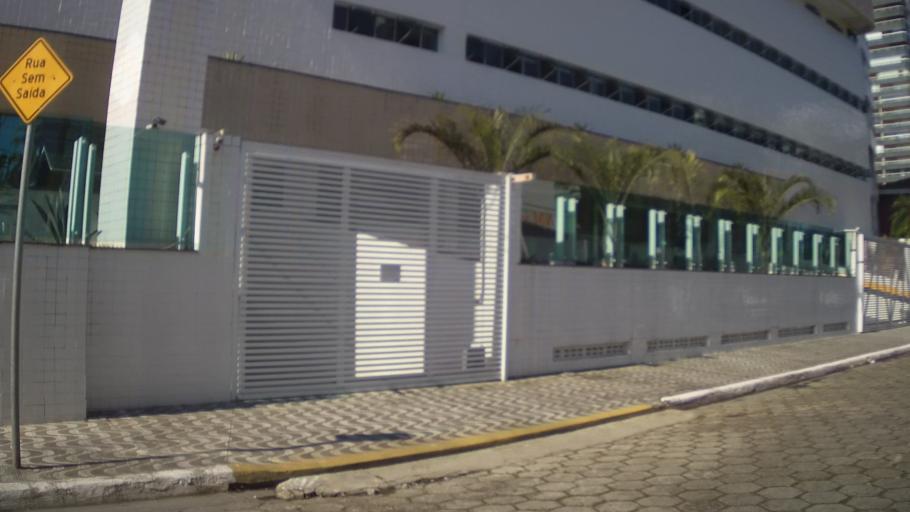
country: BR
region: Sao Paulo
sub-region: Praia Grande
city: Praia Grande
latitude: -24.0125
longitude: -46.4010
